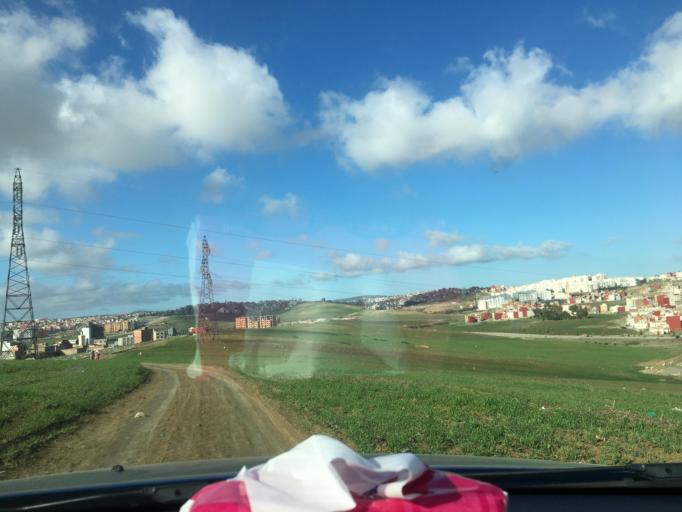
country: MA
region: Tanger-Tetouan
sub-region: Tanger-Assilah
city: Tangier
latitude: 35.7159
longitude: -5.8152
